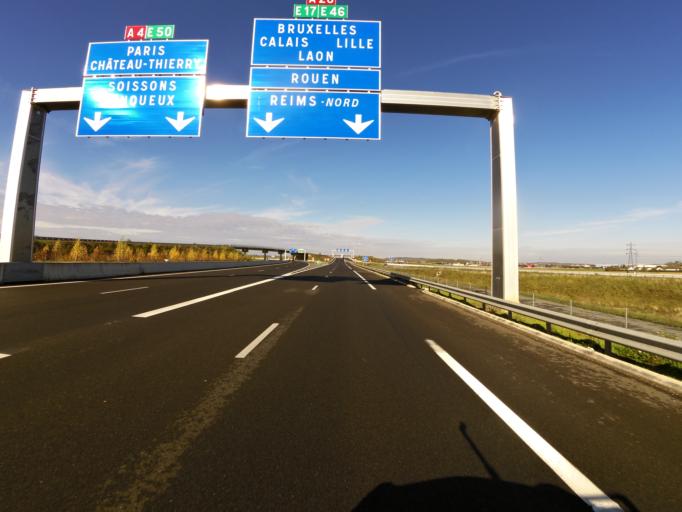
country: FR
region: Champagne-Ardenne
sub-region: Departement de la Marne
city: Tinqueux
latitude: 49.2416
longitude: 3.9671
